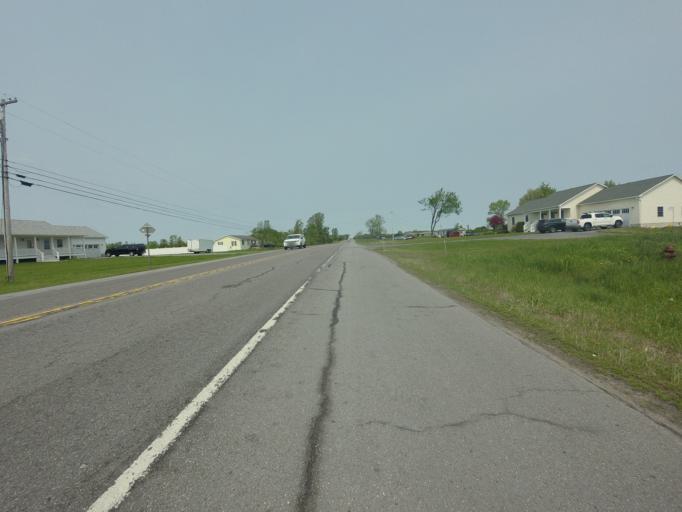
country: US
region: New York
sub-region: Jefferson County
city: Dexter
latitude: 44.0319
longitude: -76.0547
